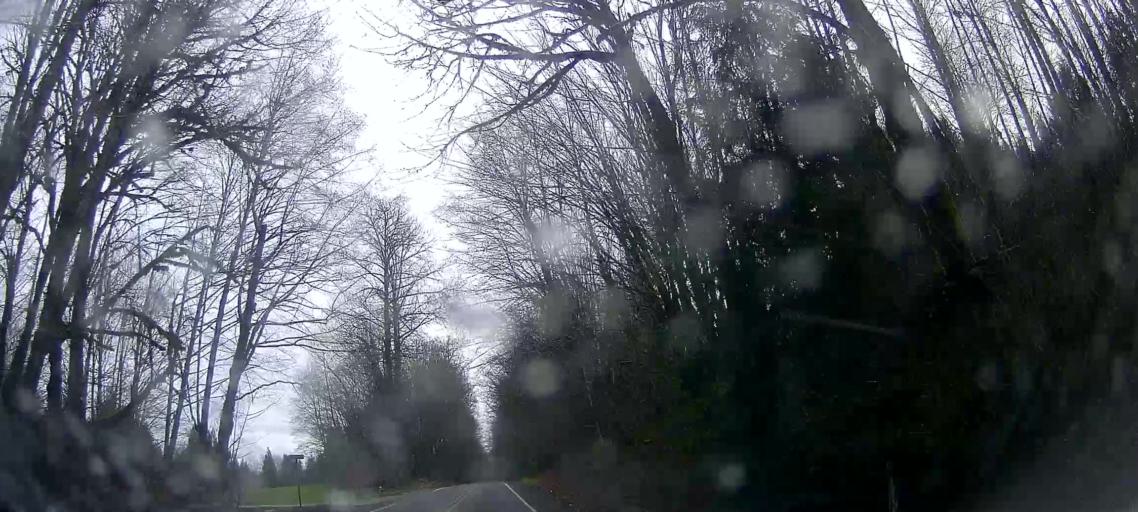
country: US
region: Washington
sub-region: Snohomish County
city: Darrington
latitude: 48.5311
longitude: -121.7878
